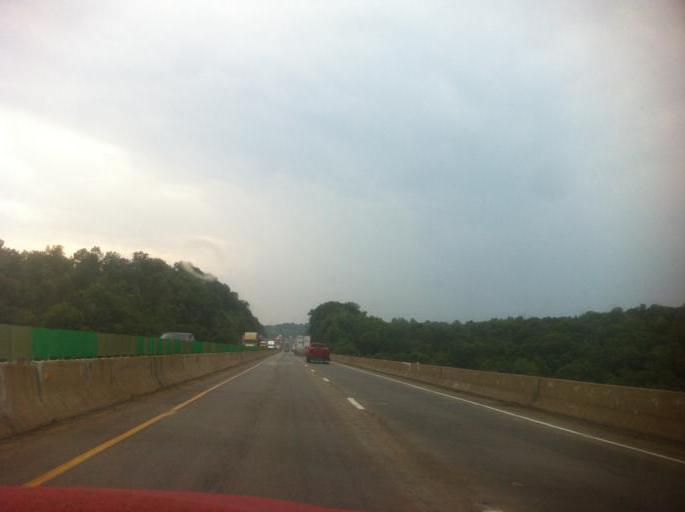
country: US
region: Pennsylvania
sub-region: Clarion County
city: Clarion
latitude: 41.1883
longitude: -79.4145
